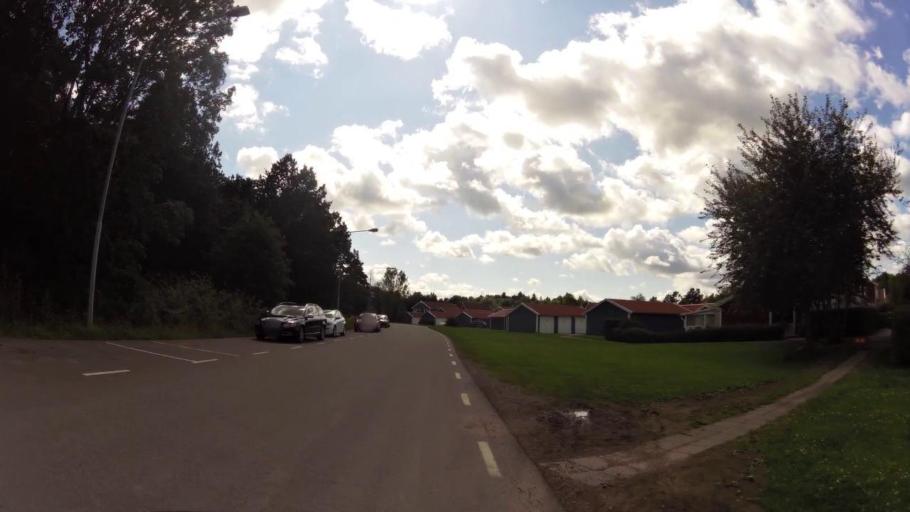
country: SE
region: OEstergoetland
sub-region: Linkopings Kommun
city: Berg
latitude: 58.4959
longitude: 15.5126
